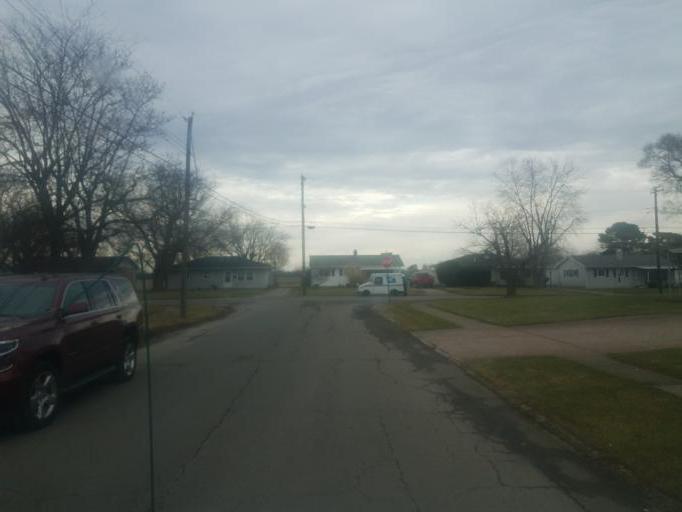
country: US
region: Ohio
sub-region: Marion County
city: Marion
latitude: 40.6021
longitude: -83.1164
